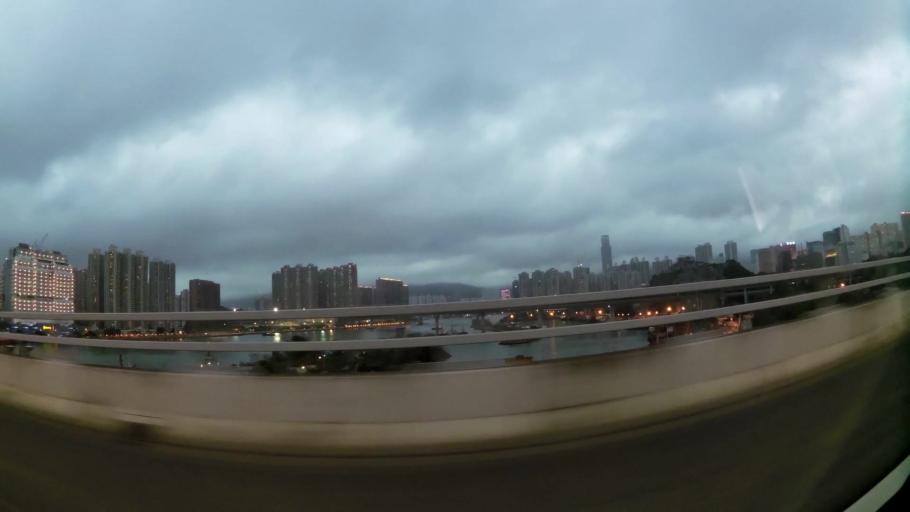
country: HK
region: Tsuen Wan
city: Tsuen Wan
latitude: 22.3506
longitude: 114.1162
